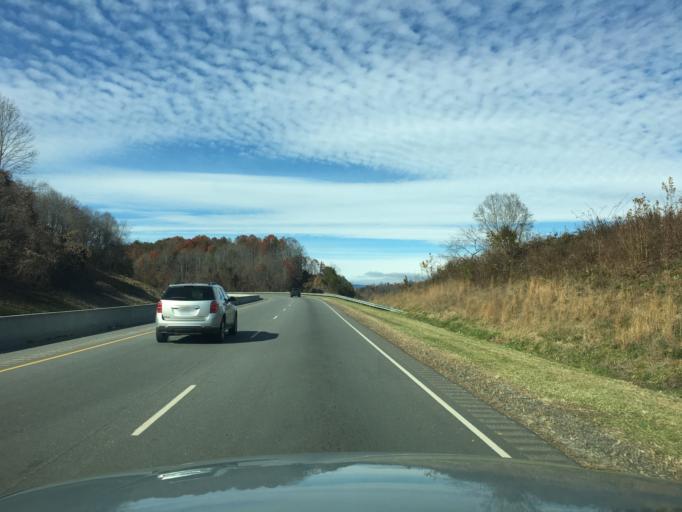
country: US
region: North Carolina
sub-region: McDowell County
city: Marion
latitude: 35.6653
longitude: -81.9812
